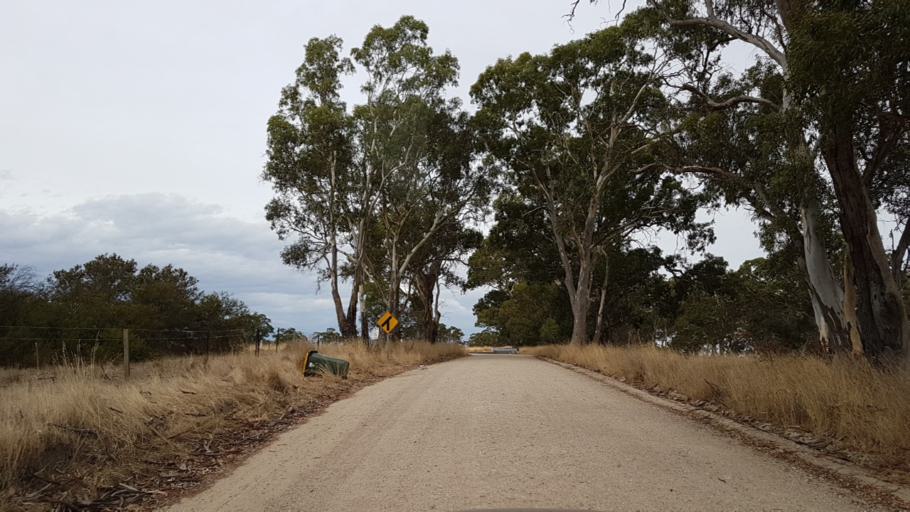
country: AU
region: South Australia
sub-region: Adelaide Hills
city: Birdwood
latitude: -34.7619
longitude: 139.0071
